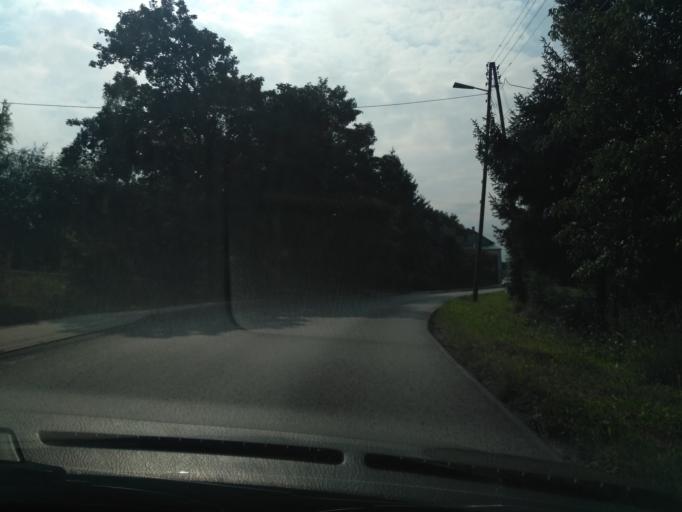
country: PL
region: Subcarpathian Voivodeship
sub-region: Powiat rzeszowski
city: Kielanowka
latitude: 50.0065
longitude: 21.9087
